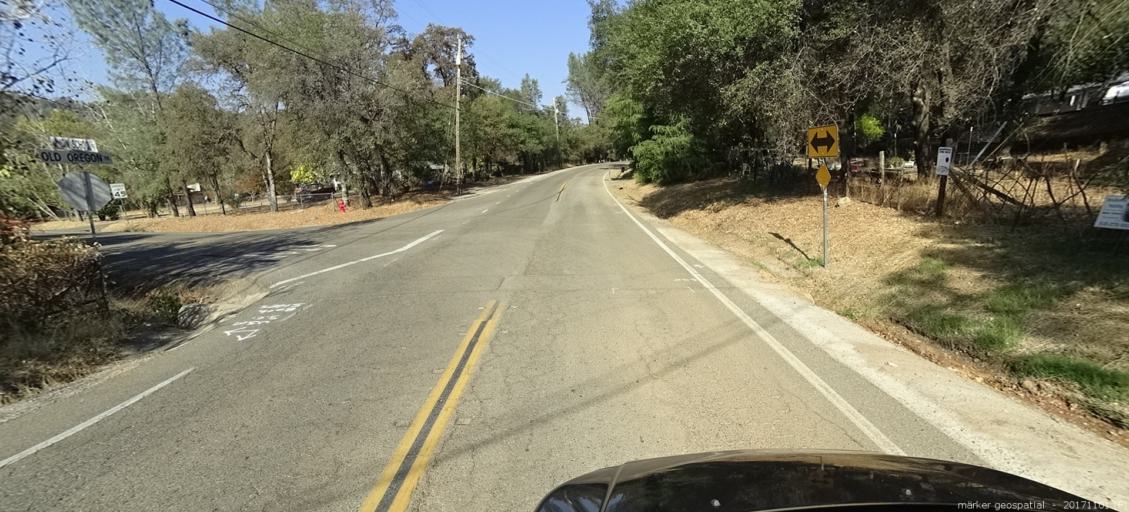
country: US
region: California
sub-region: Shasta County
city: Shasta Lake
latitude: 40.6886
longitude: -122.3175
